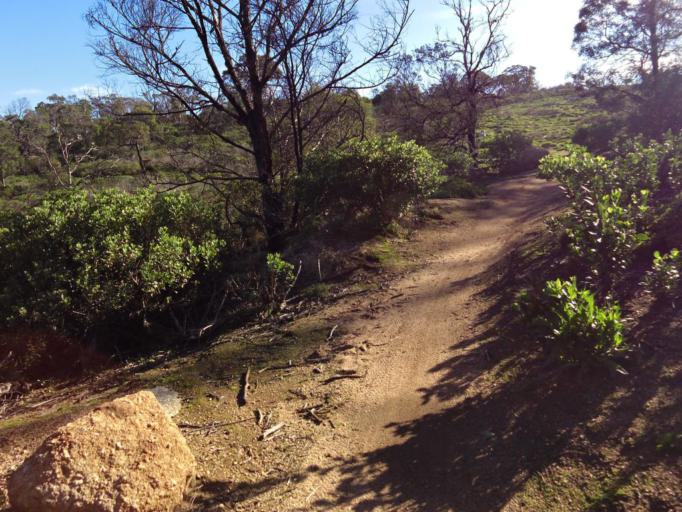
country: AU
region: Victoria
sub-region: Wyndham
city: Little River
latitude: -37.9252
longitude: 144.4367
